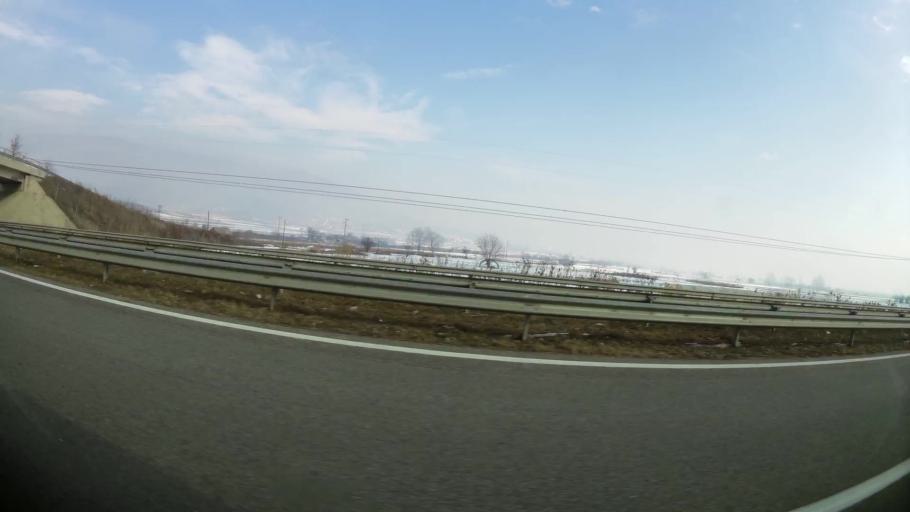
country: MK
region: Aracinovo
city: Arachinovo
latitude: 42.0257
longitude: 21.5308
